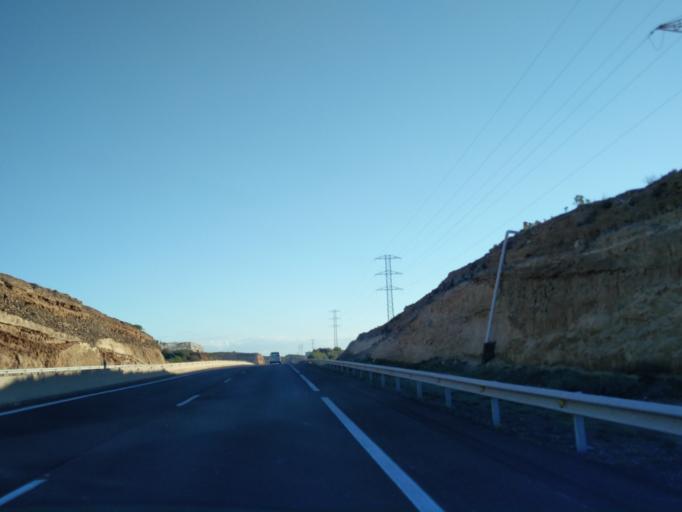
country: ES
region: Canary Islands
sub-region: Provincia de Santa Cruz de Tenerife
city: Lomo de Arico
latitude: 28.1090
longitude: -16.4882
